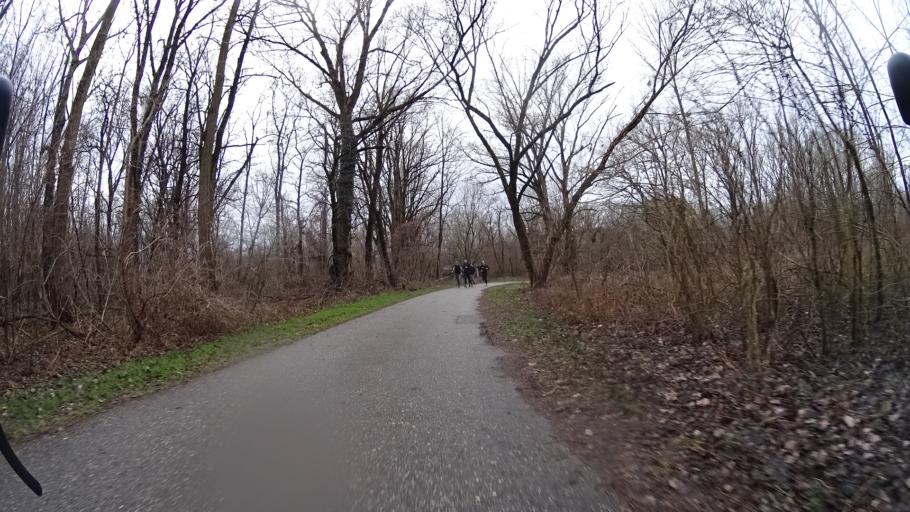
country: AT
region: Lower Austria
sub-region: Politischer Bezirk Korneuburg
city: Korneuburg
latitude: 48.3433
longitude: 16.3136
